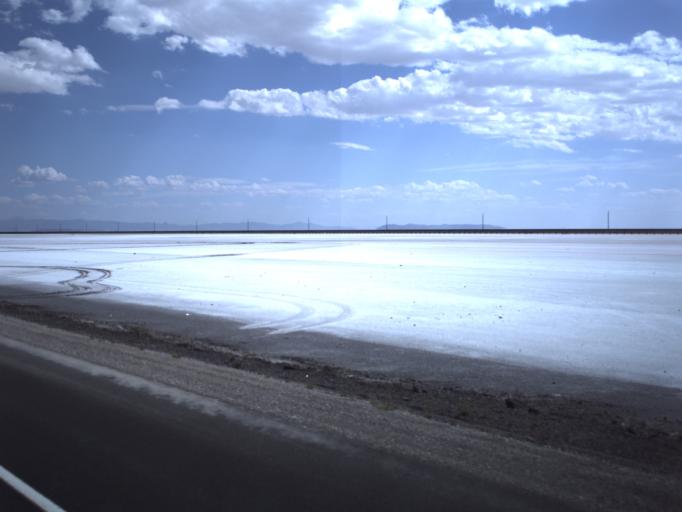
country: US
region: Utah
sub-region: Tooele County
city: Wendover
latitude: 40.7344
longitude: -113.6549
